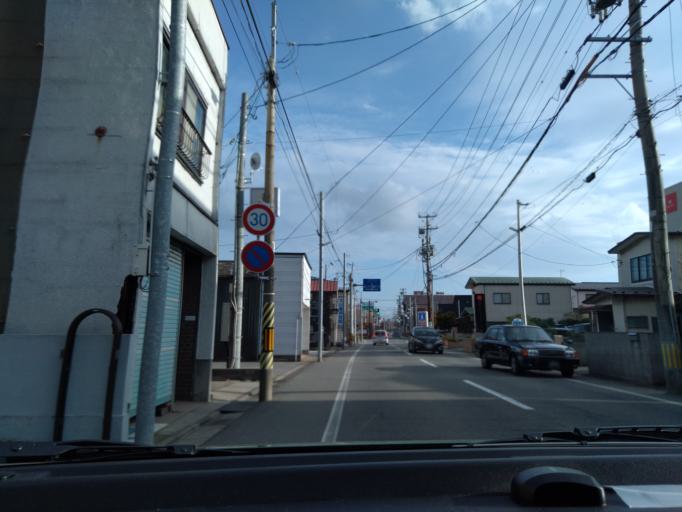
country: JP
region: Akita
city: Akita Shi
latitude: 39.7582
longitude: 140.0693
